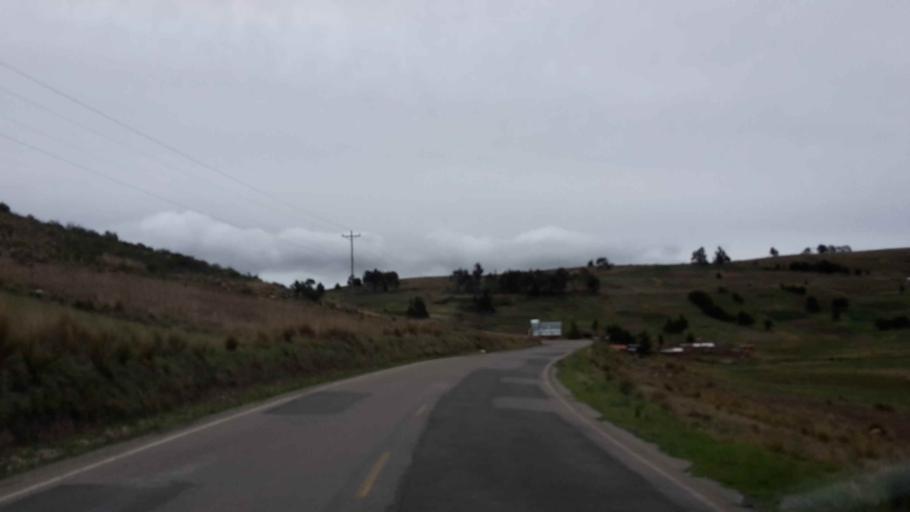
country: BO
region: Cochabamba
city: Arani
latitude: -17.4790
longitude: -65.5971
